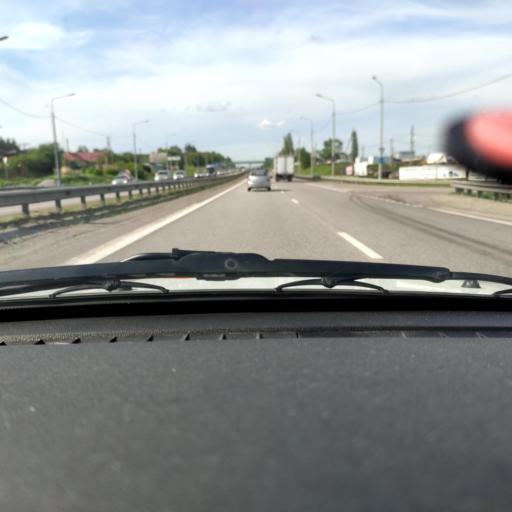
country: RU
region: Voronezj
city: Ramon'
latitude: 51.9417
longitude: 39.2218
